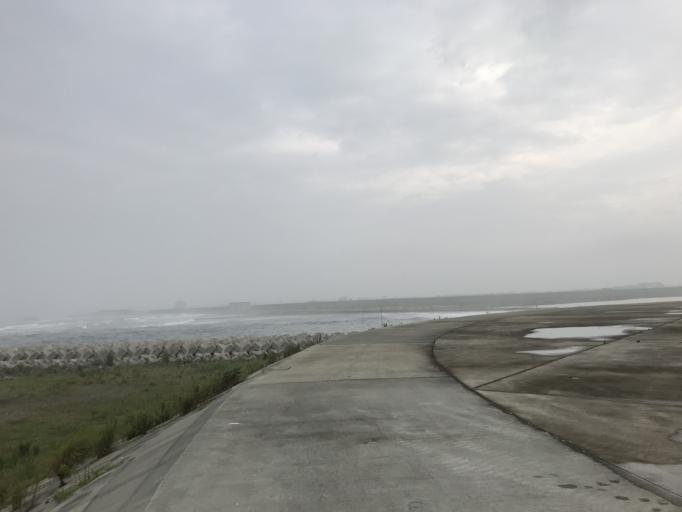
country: JP
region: Miyagi
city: Watari
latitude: 38.0511
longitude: 140.9218
